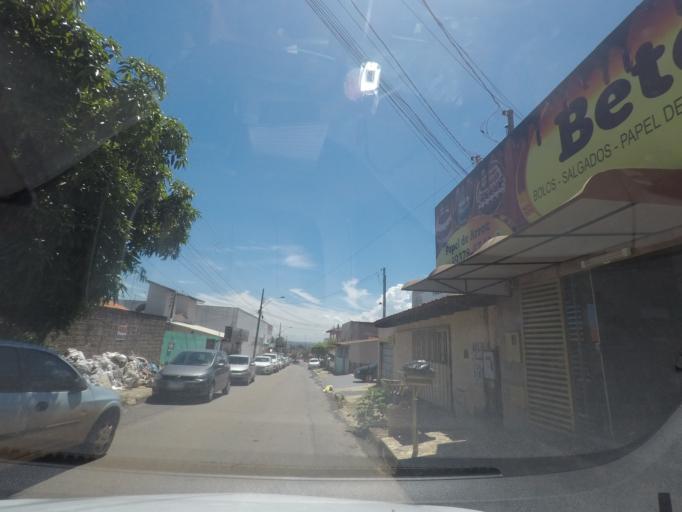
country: BR
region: Goias
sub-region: Aparecida De Goiania
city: Aparecida de Goiania
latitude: -16.7668
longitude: -49.3452
